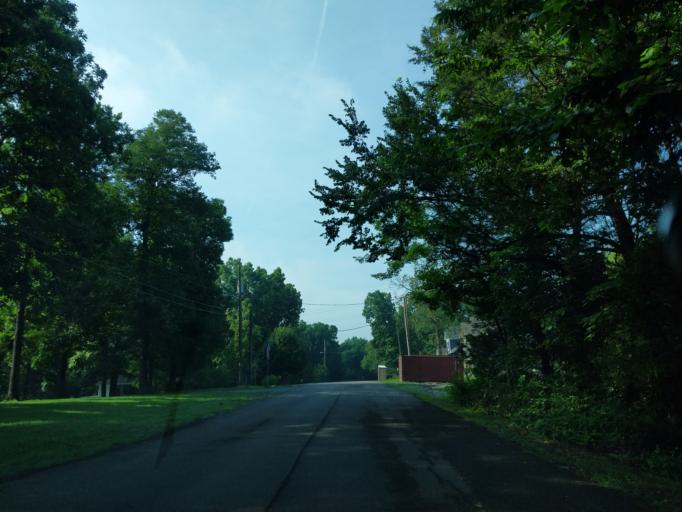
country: US
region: Tennessee
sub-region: Davidson County
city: Goodlettsville
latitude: 36.3126
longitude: -86.6901
